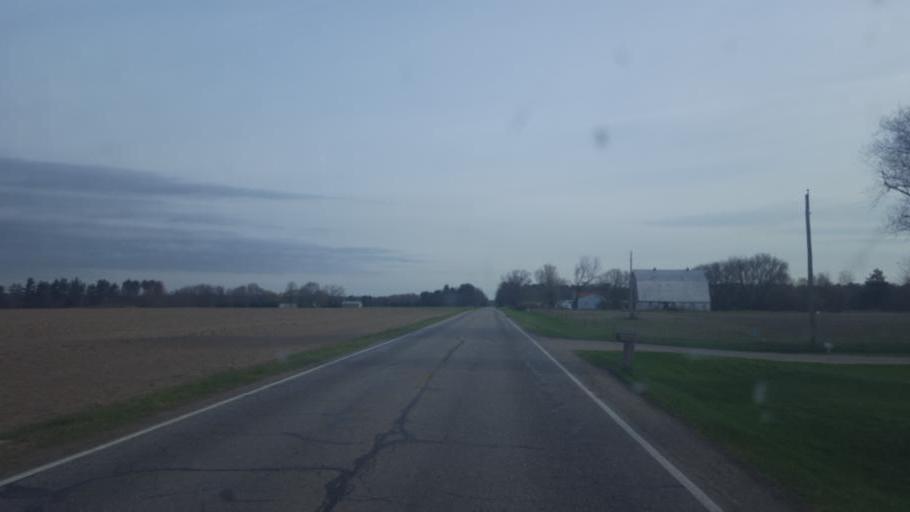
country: US
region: Michigan
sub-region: Isabella County
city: Lake Isabella
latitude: 43.5345
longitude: -84.9863
